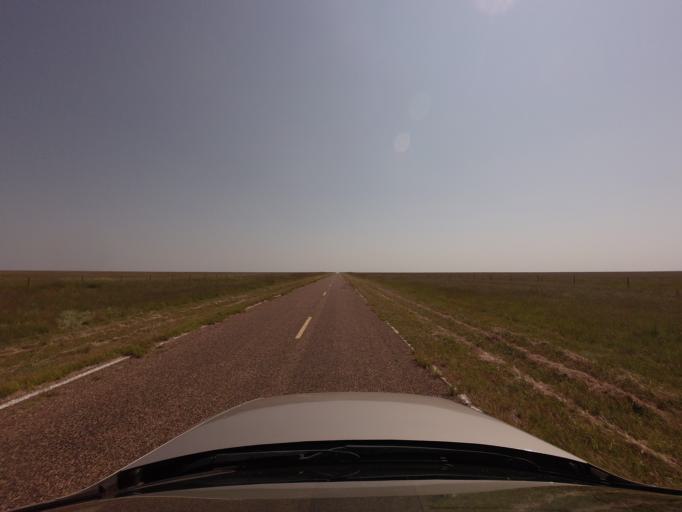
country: US
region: New Mexico
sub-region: Curry County
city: Cannon Air Force Base
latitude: 34.6333
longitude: -103.4476
